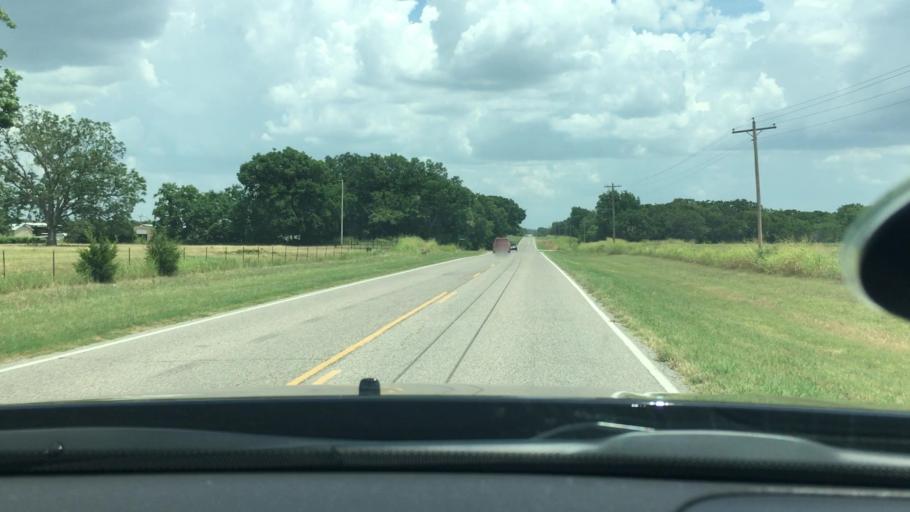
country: US
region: Oklahoma
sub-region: Love County
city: Marietta
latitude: 33.9839
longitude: -96.9541
